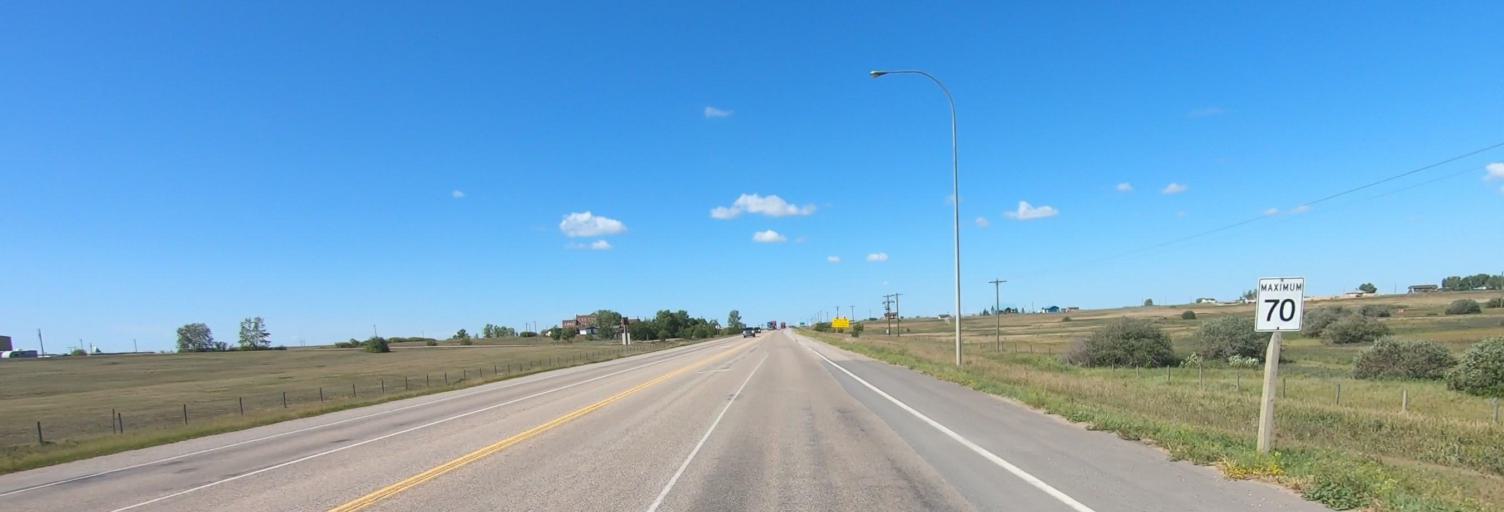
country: CA
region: Alberta
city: Strathmore
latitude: 50.8494
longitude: -113.0524
